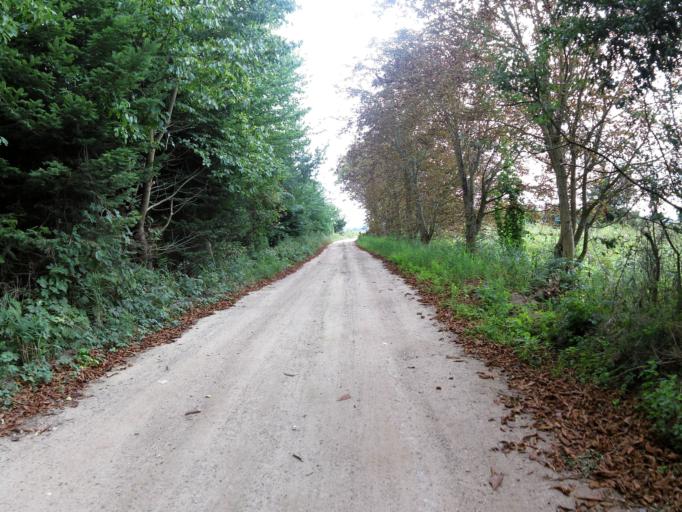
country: DE
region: Mecklenburg-Vorpommern
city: Loddin
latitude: 53.9972
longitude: 14.0609
